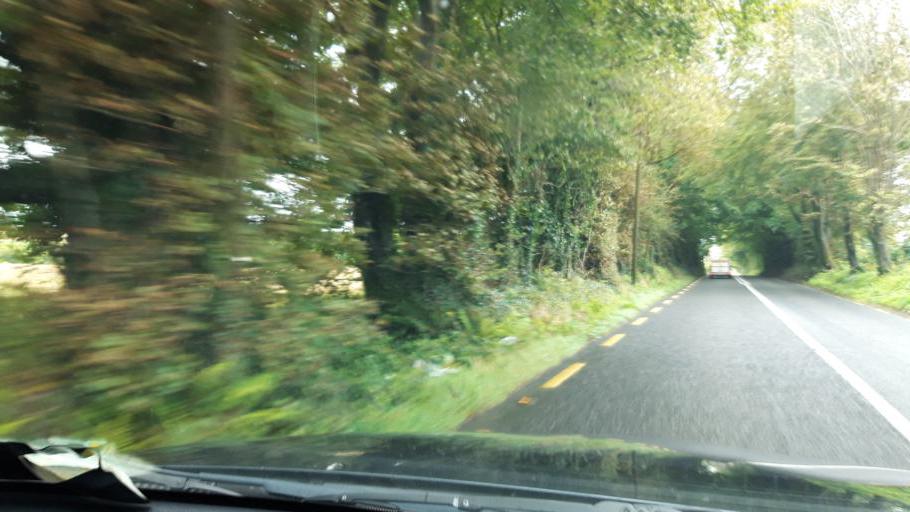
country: IE
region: Leinster
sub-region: Loch Garman
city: New Ross
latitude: 52.4341
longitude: -6.7528
